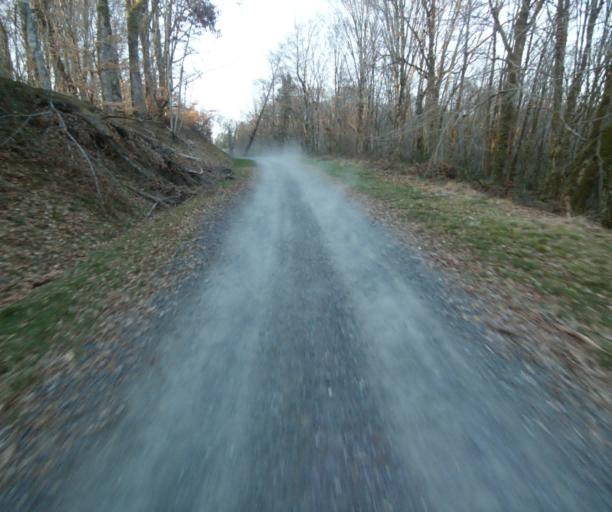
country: FR
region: Limousin
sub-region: Departement de la Correze
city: Uzerche
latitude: 45.3535
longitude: 1.6013
